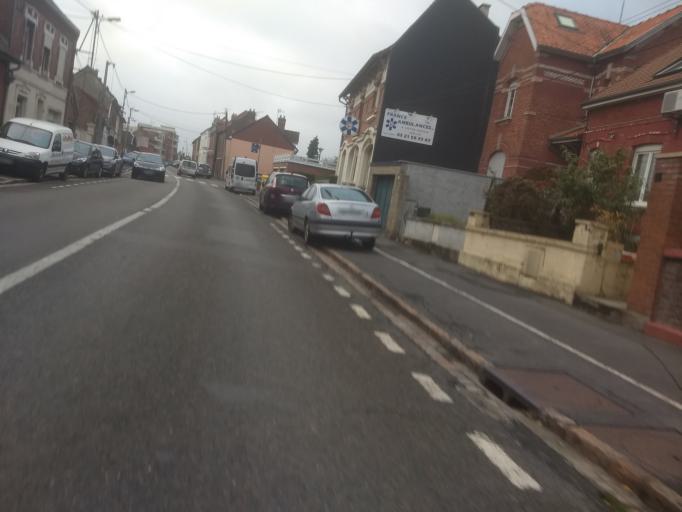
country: FR
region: Nord-Pas-de-Calais
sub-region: Departement du Pas-de-Calais
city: Saint-Laurent-Blangy
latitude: 50.3006
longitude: 2.7984
